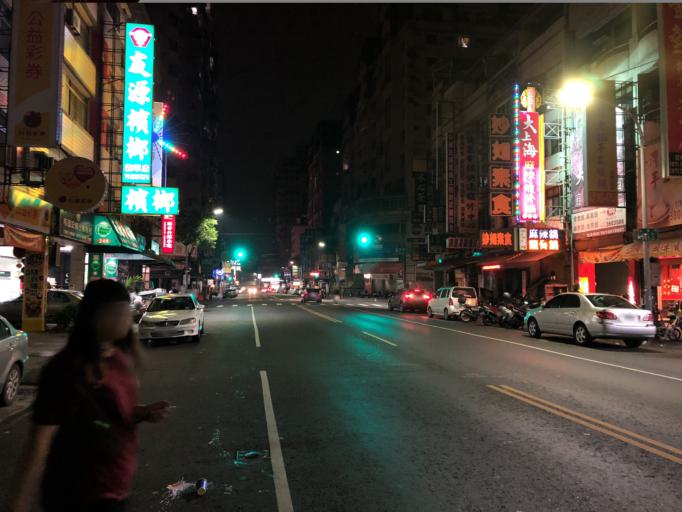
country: TW
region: Taiwan
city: Fengshan
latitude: 22.6434
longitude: 120.3343
